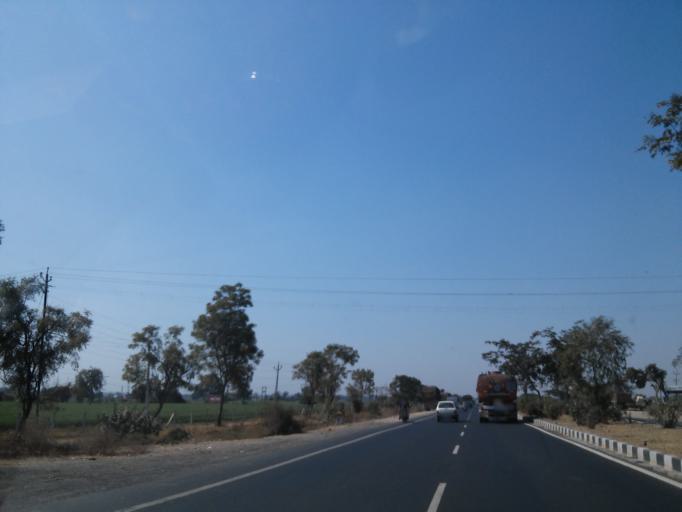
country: IN
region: Gujarat
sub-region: Sabar Kantha
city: Himatnagar
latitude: 23.5828
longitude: 73.0189
